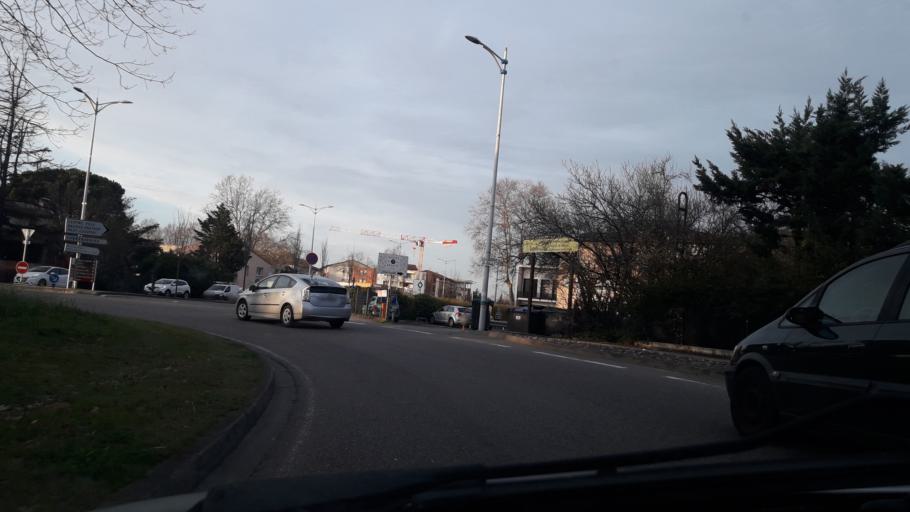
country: FR
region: Midi-Pyrenees
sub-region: Departement de la Haute-Garonne
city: Colomiers
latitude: 43.6069
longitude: 1.3359
